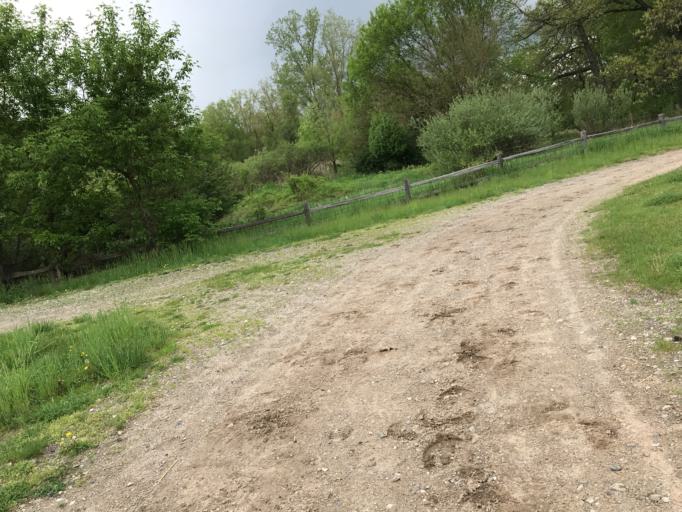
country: US
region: Michigan
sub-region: Oakland County
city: Milford
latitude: 42.5526
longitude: -83.6321
